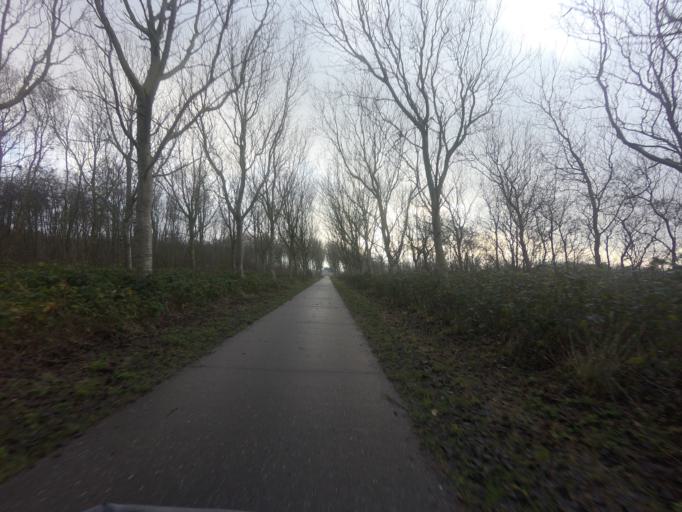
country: NL
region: North Holland
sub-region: Gemeente Texel
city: Den Burg
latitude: 53.1605
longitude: 4.8525
